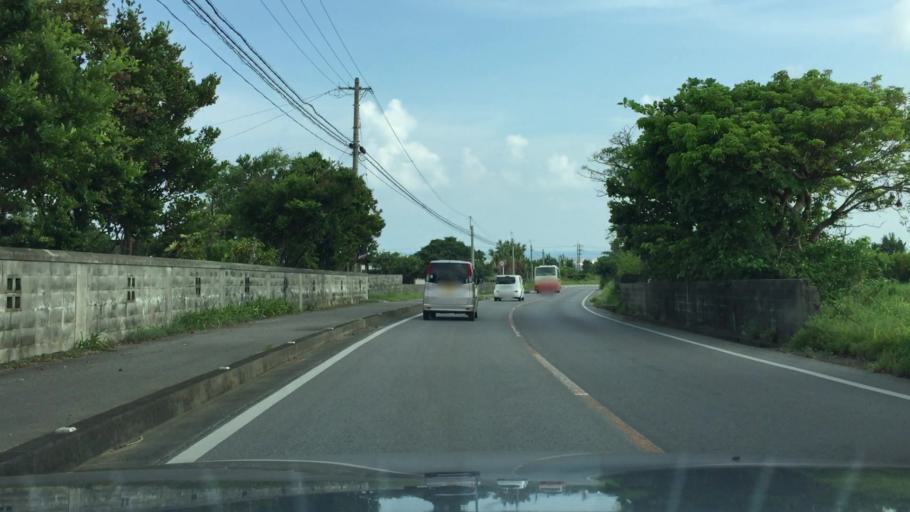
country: JP
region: Okinawa
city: Ishigaki
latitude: 24.3546
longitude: 124.1740
